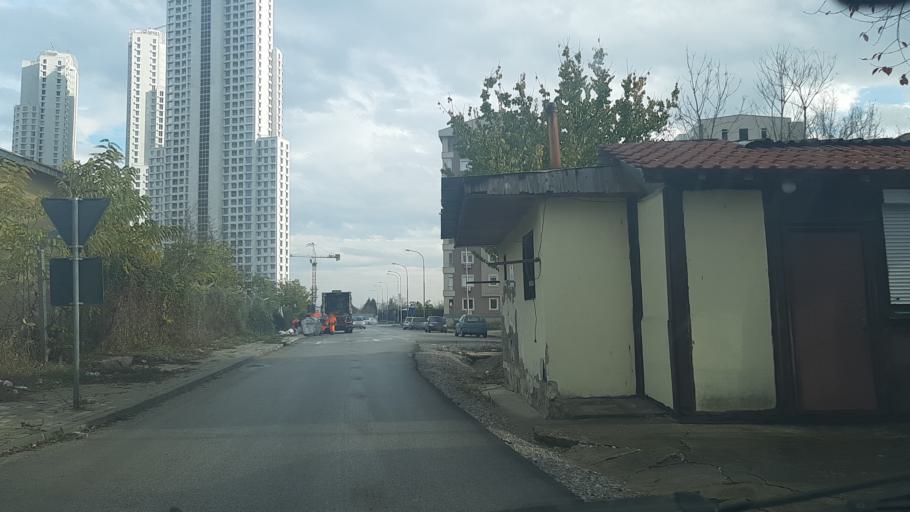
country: MK
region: Kisela Voda
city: Usje
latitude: 41.9804
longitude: 21.4613
